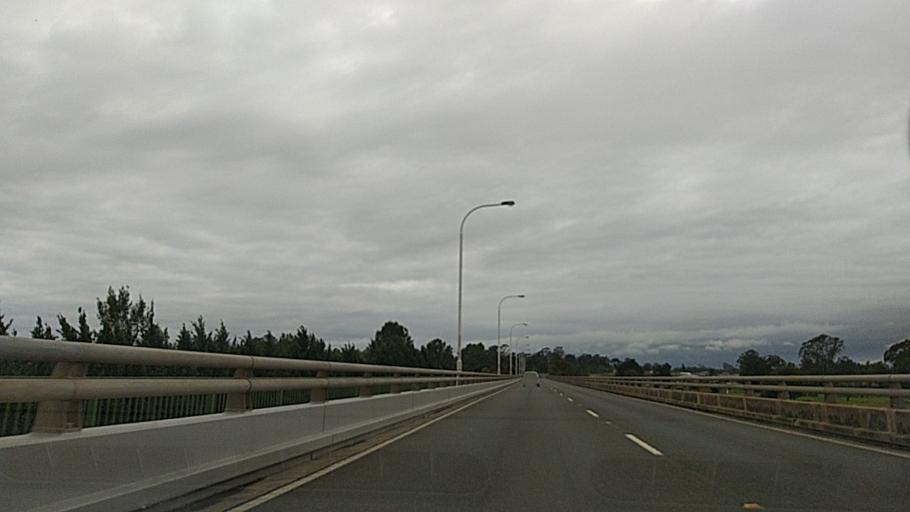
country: AU
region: New South Wales
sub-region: Camden
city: Camden South
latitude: -34.0686
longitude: 150.7057
